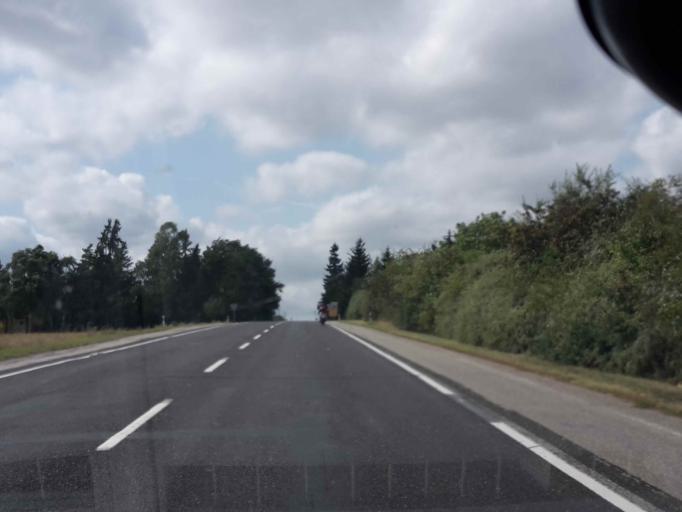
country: CZ
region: South Moravian
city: Vinicne Sumice
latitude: 49.1856
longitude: 16.8296
